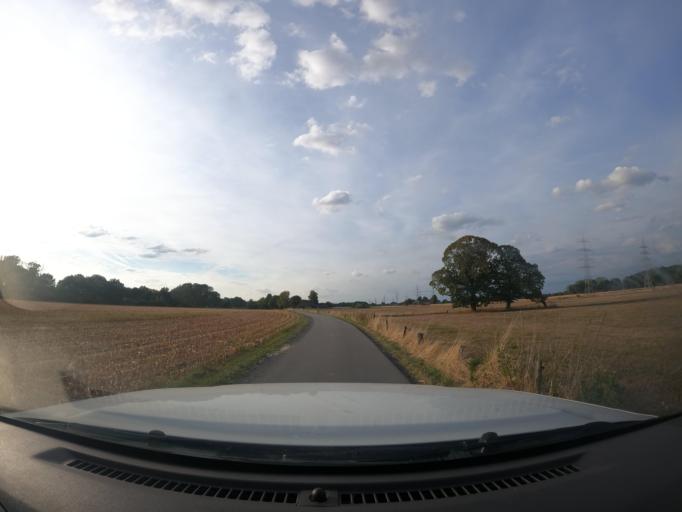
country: DE
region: North Rhine-Westphalia
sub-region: Regierungsbezirk Dusseldorf
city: Hamminkeln
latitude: 51.7045
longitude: 6.5845
